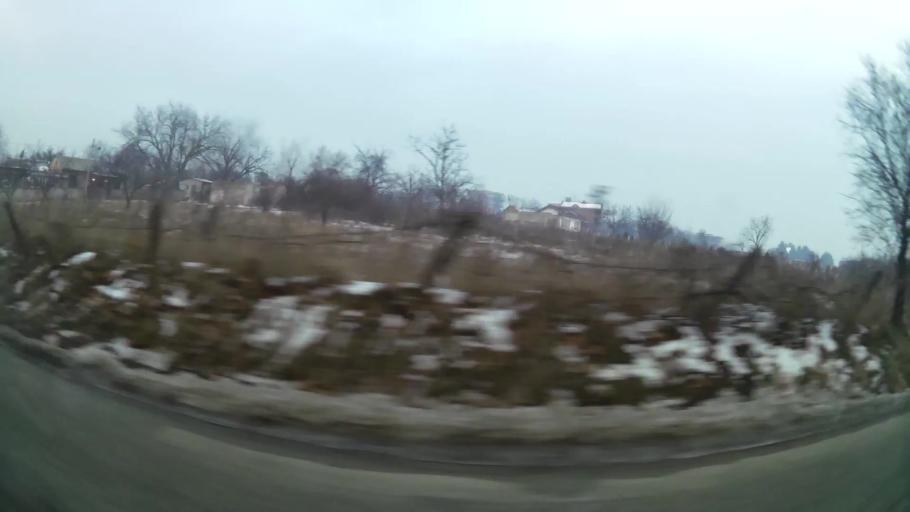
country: MK
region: Suto Orizari
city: Suto Orizare
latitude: 42.0314
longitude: 21.4072
